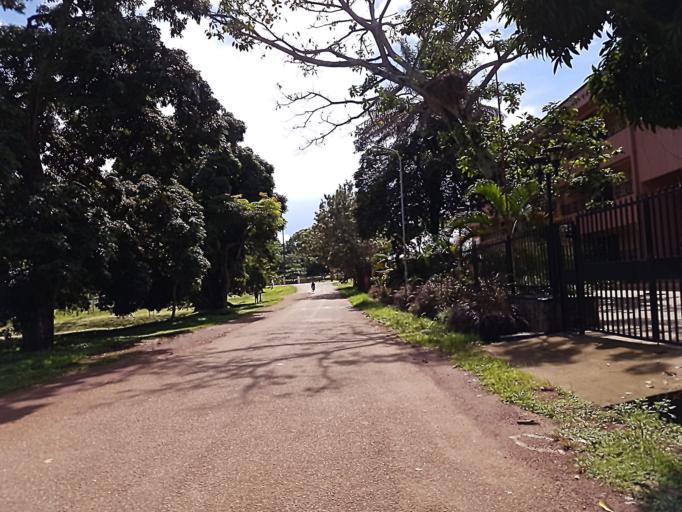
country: UG
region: Central Region
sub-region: Wakiso District
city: Entebbe
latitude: 0.0574
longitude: 32.4739
